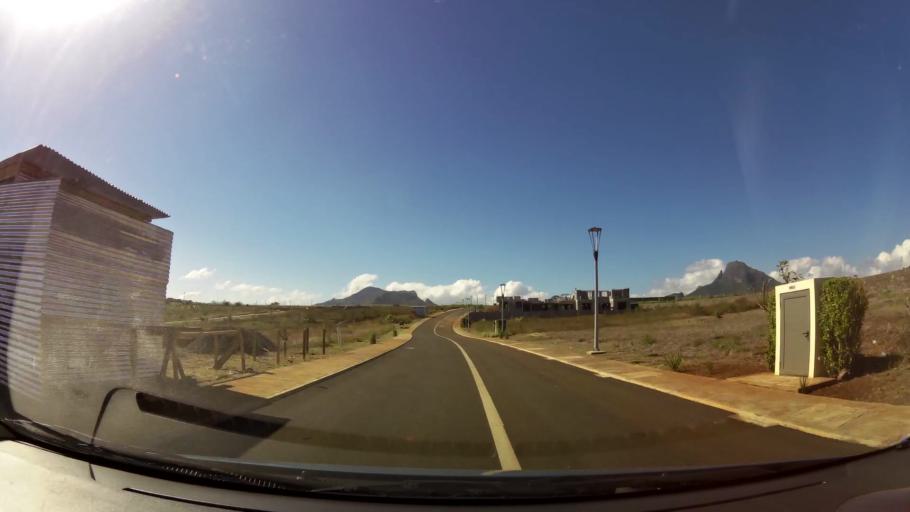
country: MU
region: Black River
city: Flic en Flac
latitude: -20.2708
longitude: 57.3831
